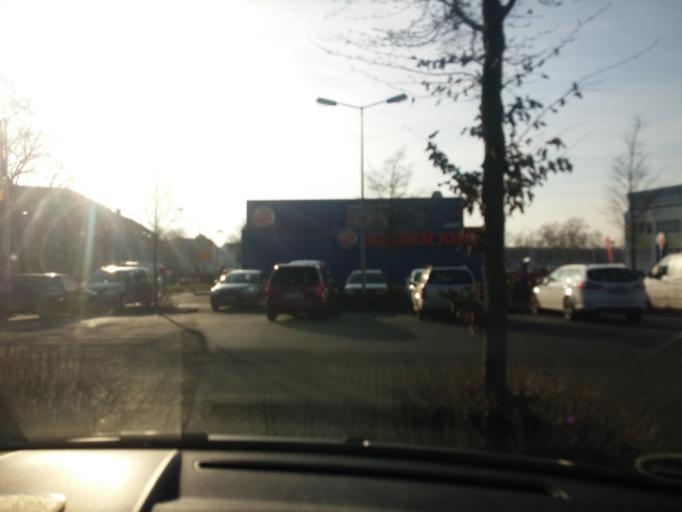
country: DE
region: Hesse
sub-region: Regierungsbezirk Darmstadt
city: Darmstadt
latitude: 49.8826
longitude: 8.6462
